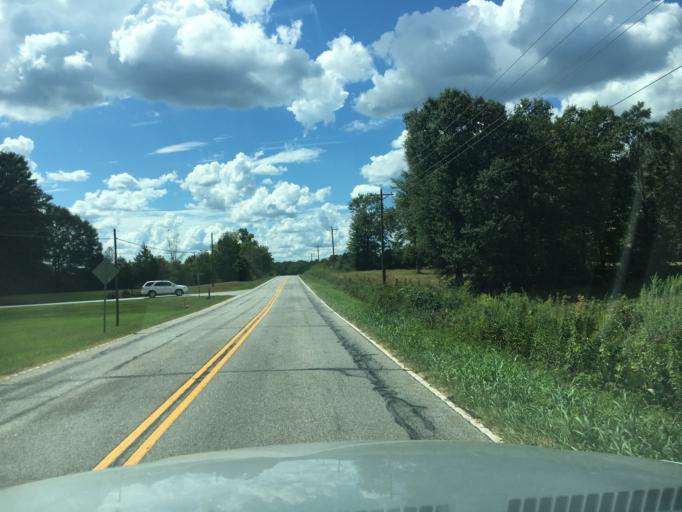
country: US
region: South Carolina
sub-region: Laurens County
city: Laurens
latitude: 34.5180
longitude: -82.1019
